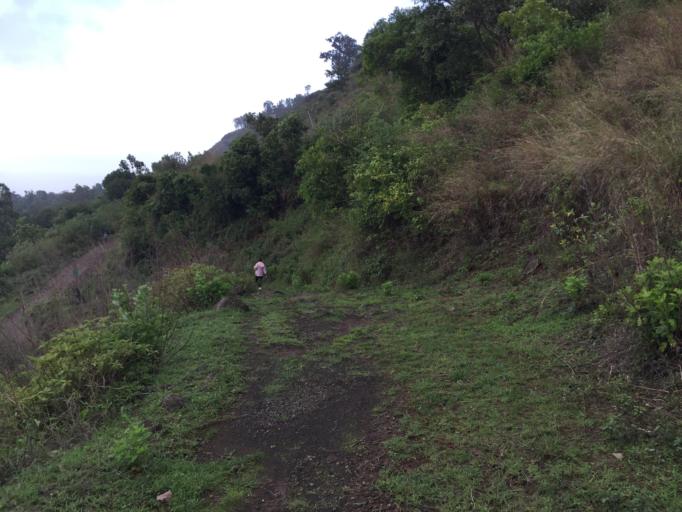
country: IN
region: Maharashtra
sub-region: Satara Division
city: Panchgani
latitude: 17.9298
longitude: 73.7575
